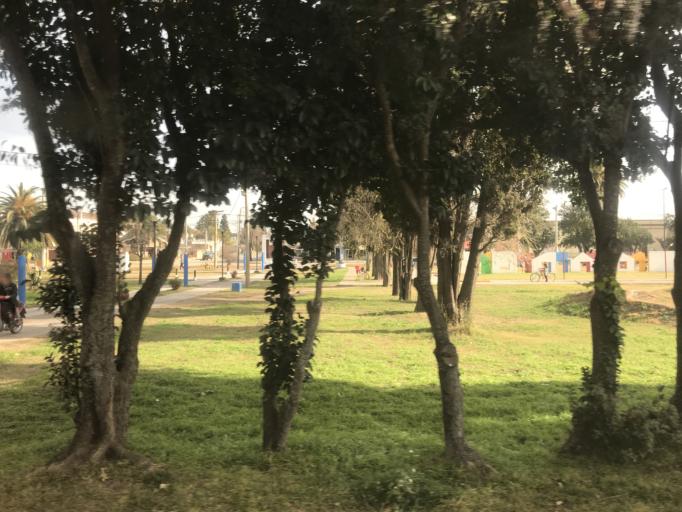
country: AR
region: Cordoba
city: Laguna Larga
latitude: -31.7771
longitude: -63.8030
